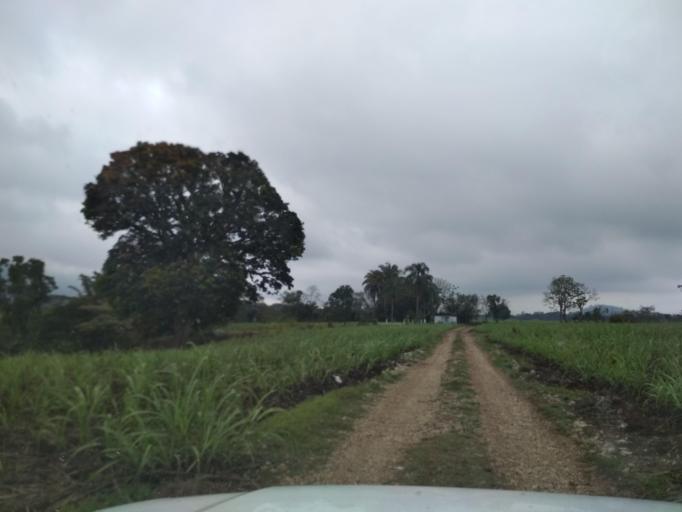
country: MX
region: Veracruz
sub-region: Cordoba
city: San Jose de Tapia
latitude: 18.8485
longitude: -96.9695
